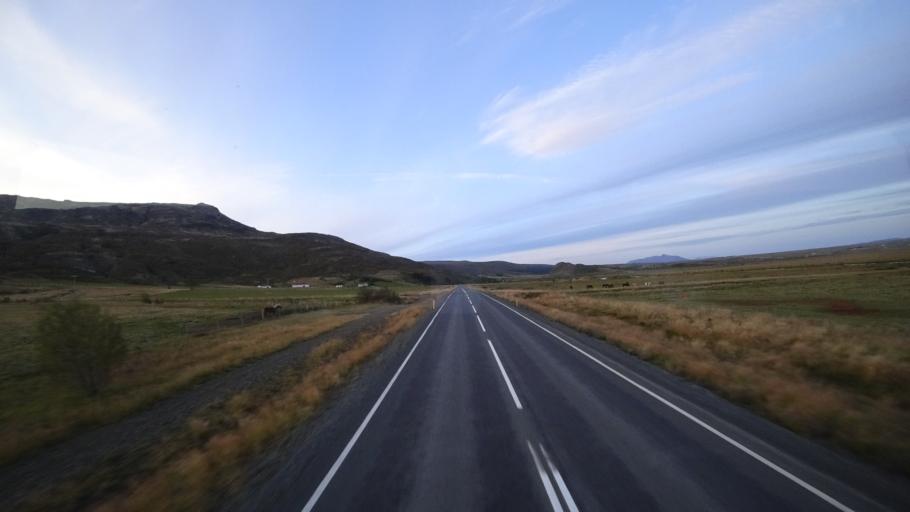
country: IS
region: South
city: Selfoss
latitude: 64.2960
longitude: -20.3338
